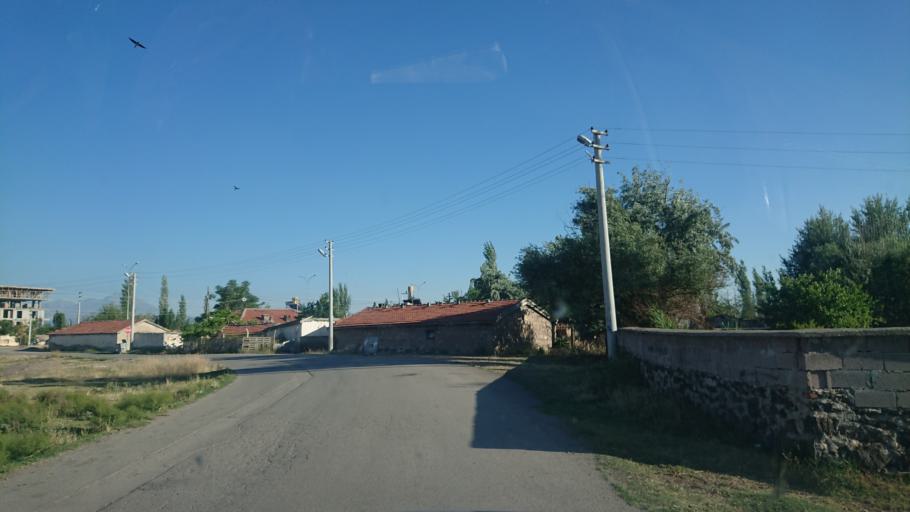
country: TR
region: Aksaray
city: Aksaray
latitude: 38.3828
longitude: 33.9912
